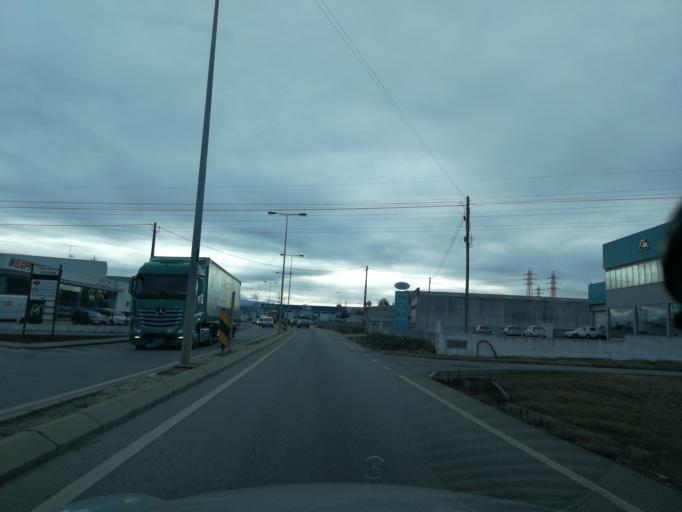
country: PT
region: Aveiro
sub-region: Agueda
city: Valongo
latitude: 40.5947
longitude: -8.4647
